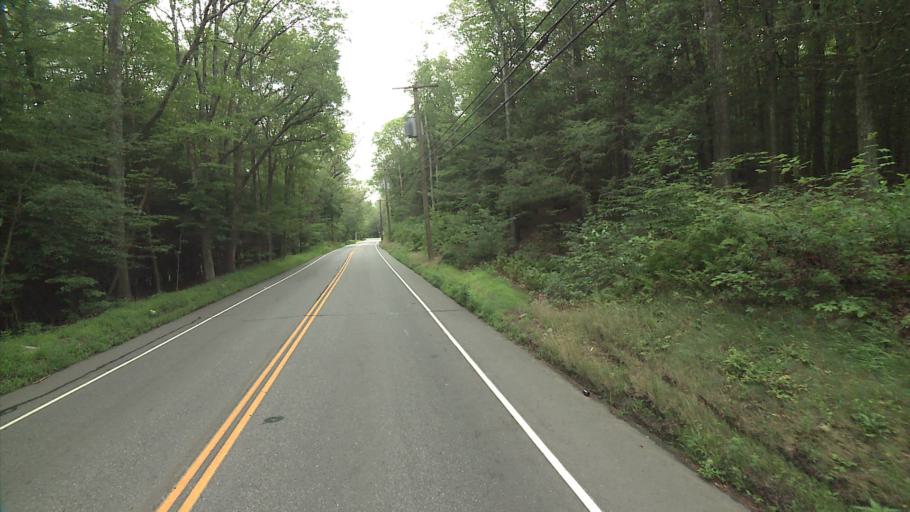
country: US
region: Connecticut
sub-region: Tolland County
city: Storrs
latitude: 41.8727
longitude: -72.2560
